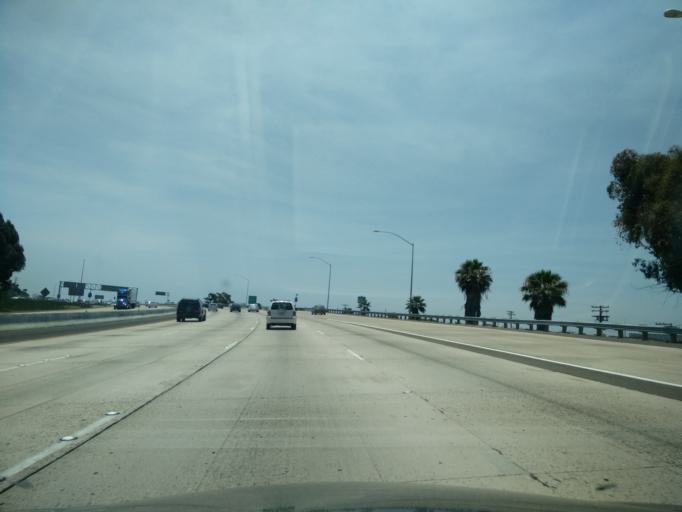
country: US
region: California
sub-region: San Diego County
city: San Diego
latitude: 32.7571
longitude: -117.2035
